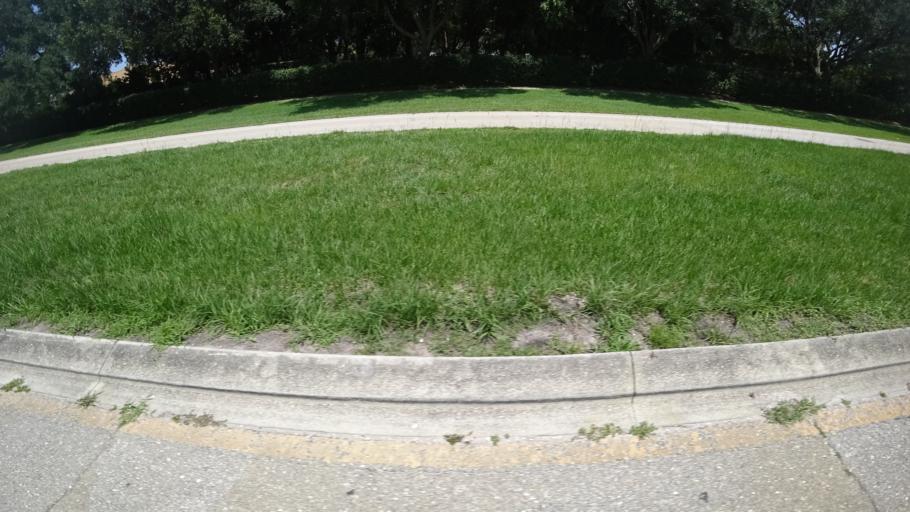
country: US
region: Florida
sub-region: Sarasota County
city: Desoto Lakes
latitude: 27.4140
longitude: -82.4714
